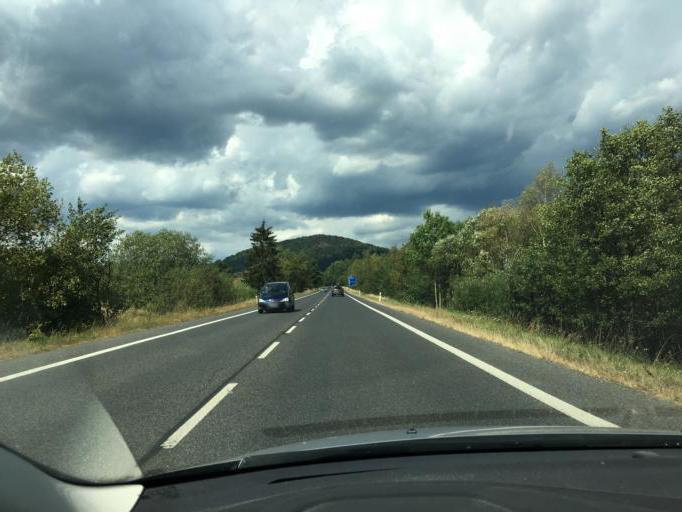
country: CZ
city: Cvikov
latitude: 50.7862
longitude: 14.6113
